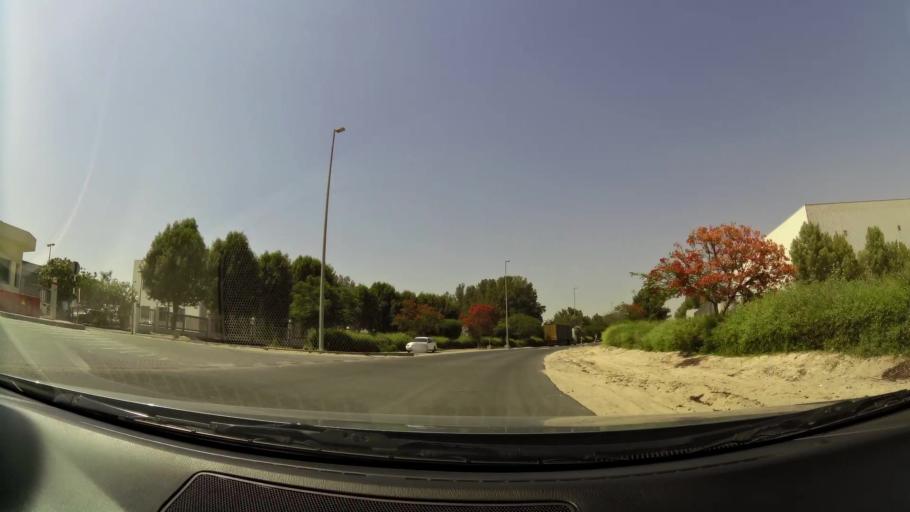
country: AE
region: Dubai
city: Dubai
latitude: 24.9786
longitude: 55.1463
